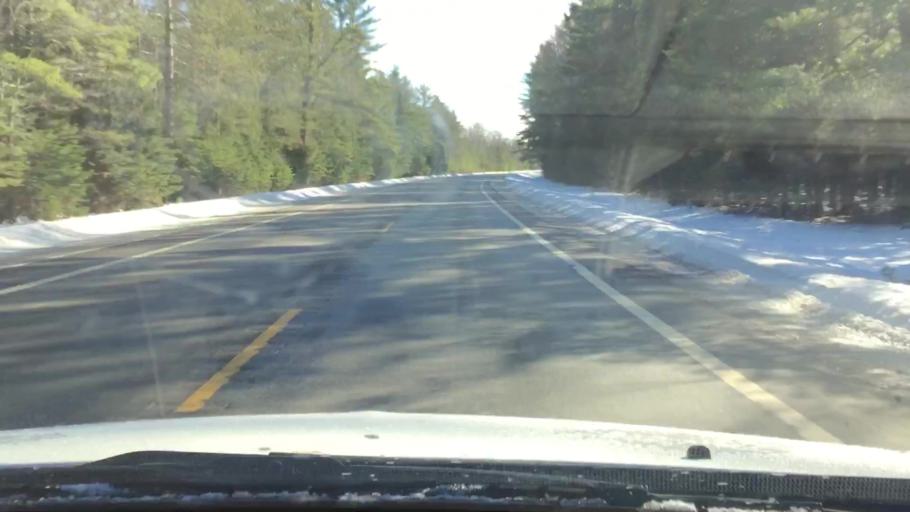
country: US
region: Michigan
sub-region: Charlevoix County
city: East Jordan
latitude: 45.0533
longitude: -85.0716
